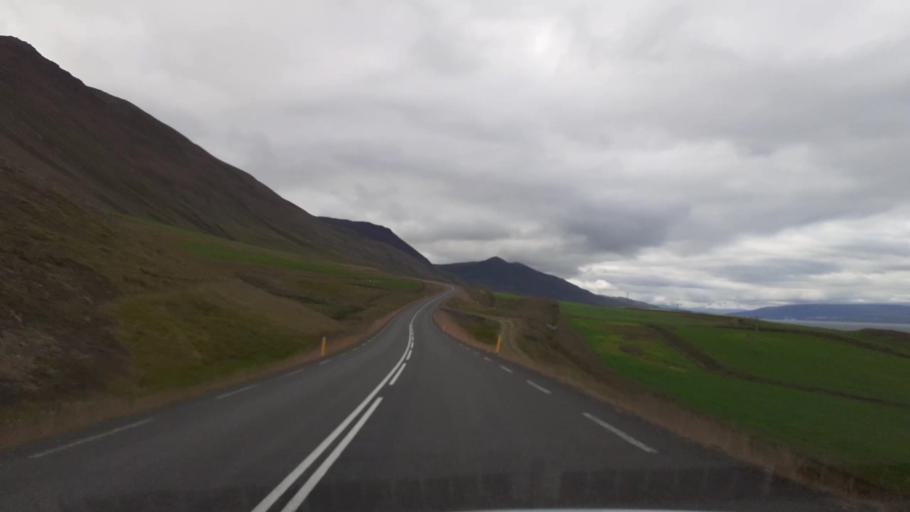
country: IS
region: Northeast
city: Akureyri
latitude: 65.8670
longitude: -18.0752
